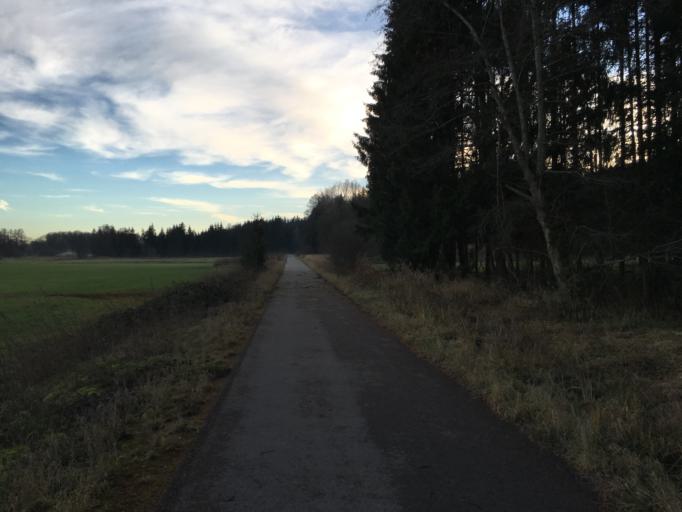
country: DE
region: Bavaria
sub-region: Swabia
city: Wald
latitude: 47.9907
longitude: 10.2864
